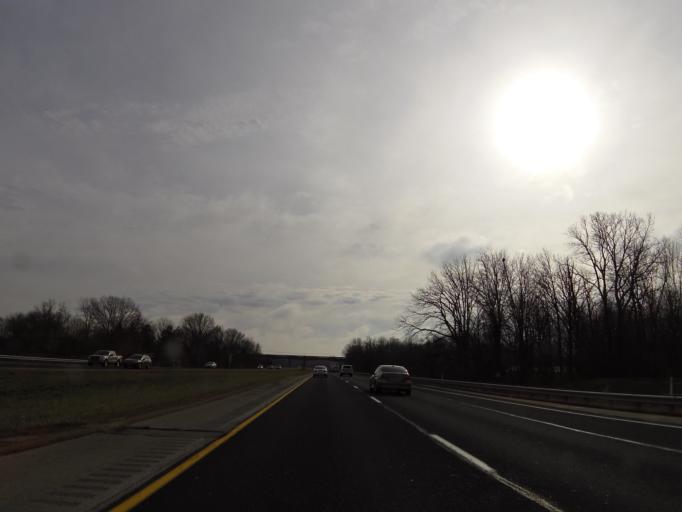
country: US
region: Indiana
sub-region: Marion County
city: Cumberland
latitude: 39.7116
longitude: -86.0041
